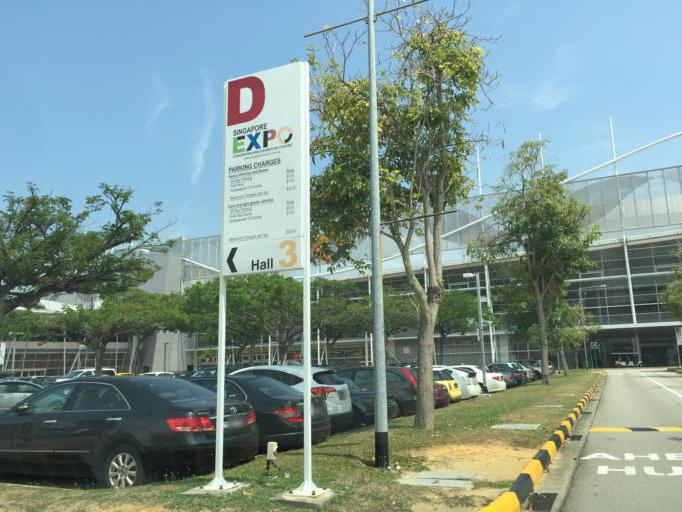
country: SG
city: Singapore
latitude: 1.3344
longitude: 103.9584
